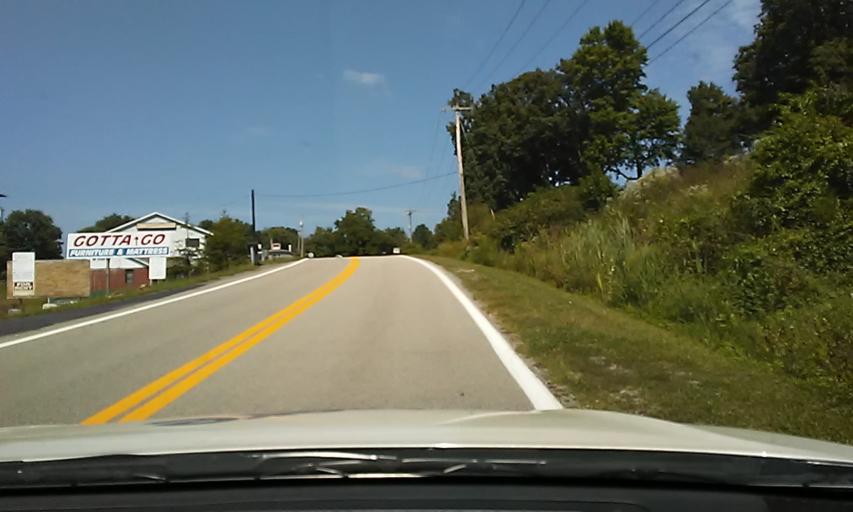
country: US
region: West Virginia
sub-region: Monongalia County
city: Westover
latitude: 39.6288
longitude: -79.9925
